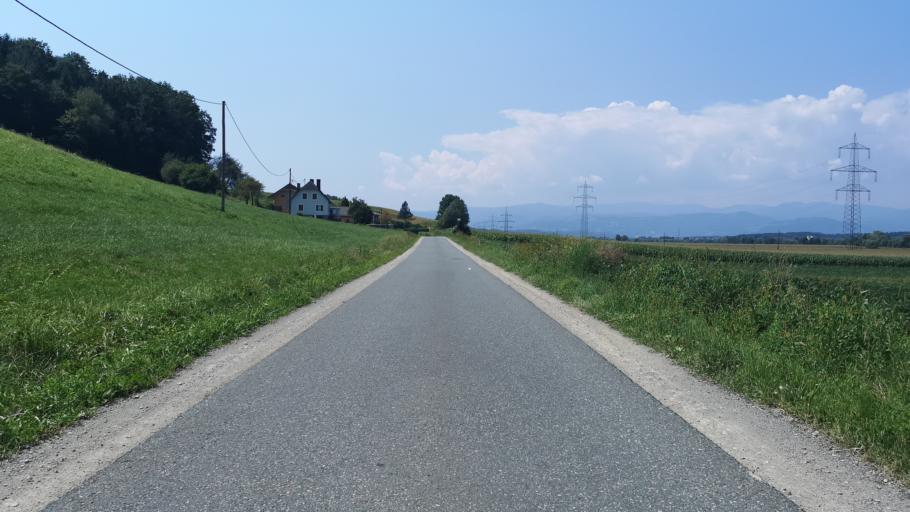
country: AT
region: Styria
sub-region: Politischer Bezirk Deutschlandsberg
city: Wettmannstatten
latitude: 46.8301
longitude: 15.3793
